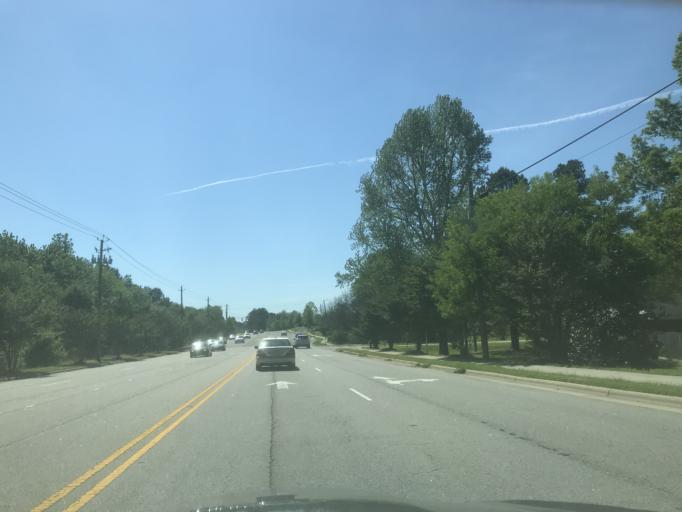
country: US
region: North Carolina
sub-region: Wake County
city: West Raleigh
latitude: 35.7488
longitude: -78.7186
